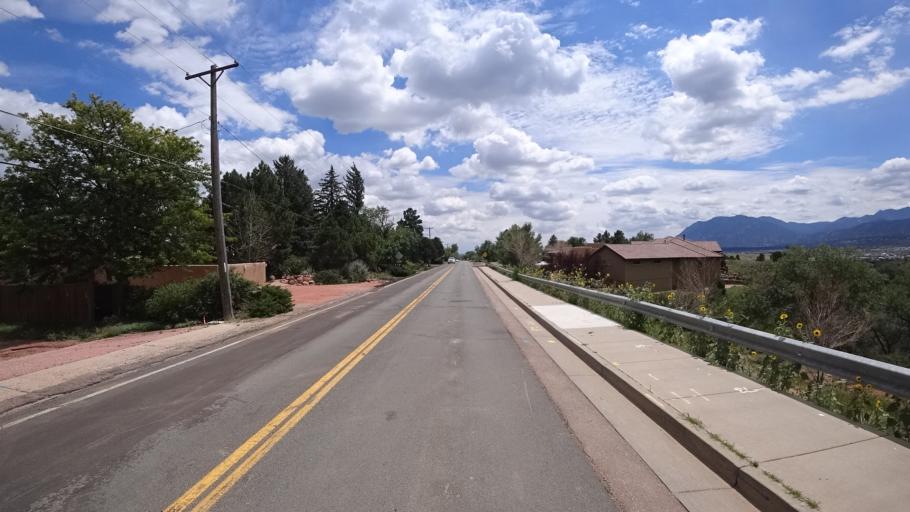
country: US
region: Colorado
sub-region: El Paso County
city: Colorado Springs
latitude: 38.8586
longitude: -104.8475
